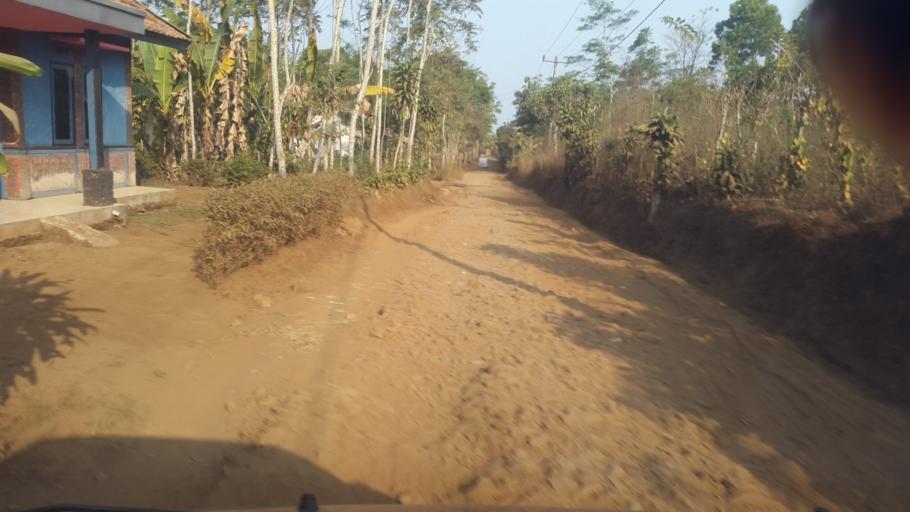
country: ID
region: West Java
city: Sindangraja
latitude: -7.1208
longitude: 106.9338
